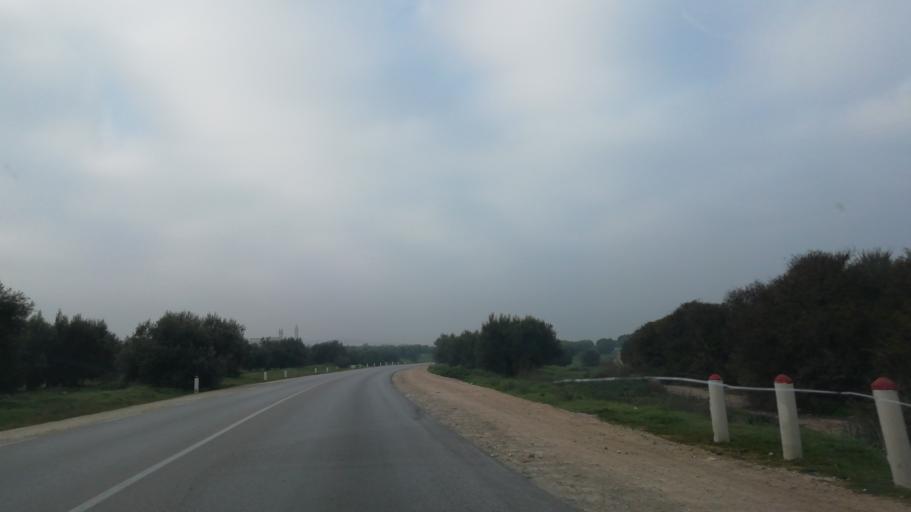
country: DZ
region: Relizane
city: Djidiouia
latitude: 35.9385
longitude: 0.8569
